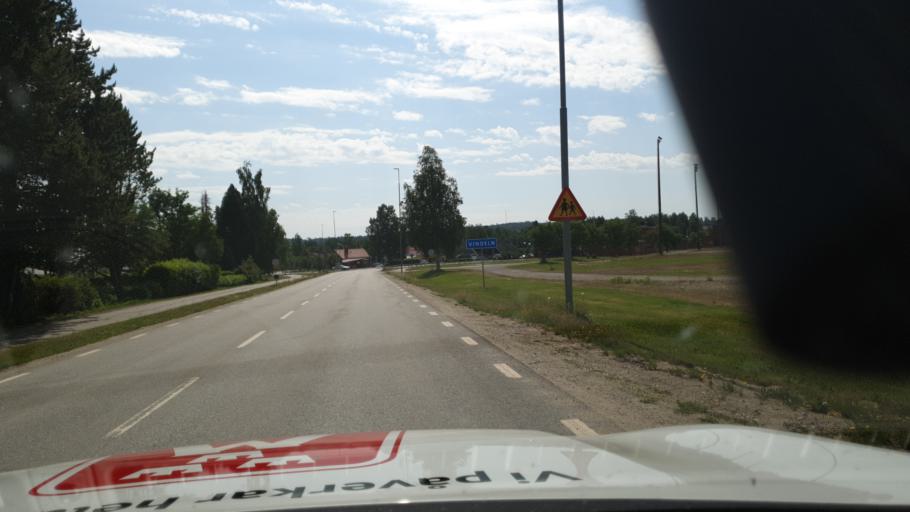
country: SE
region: Vaesterbotten
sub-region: Vindelns Kommun
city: Vindeln
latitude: 64.2086
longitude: 19.7185
